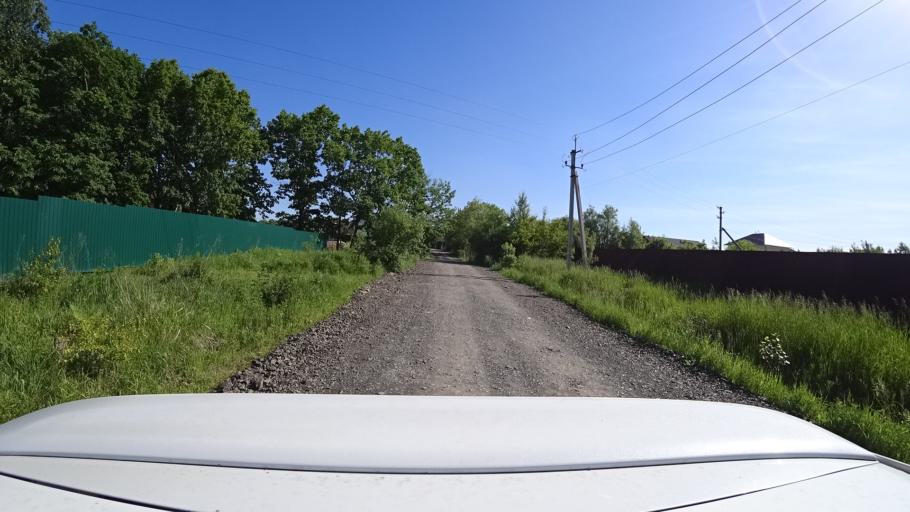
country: RU
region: Khabarovsk Krai
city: Topolevo
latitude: 48.5489
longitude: 135.1828
